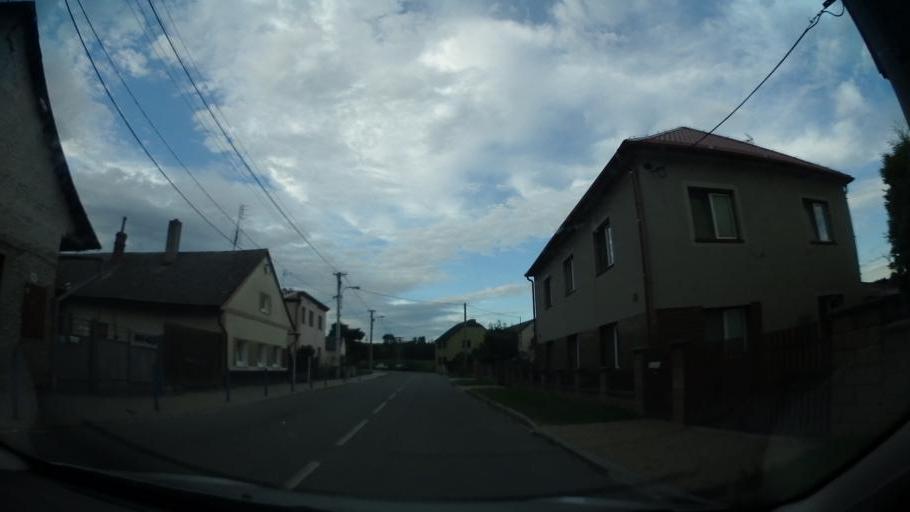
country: CZ
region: Olomoucky
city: Bila Lhota
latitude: 49.7065
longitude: 17.0204
